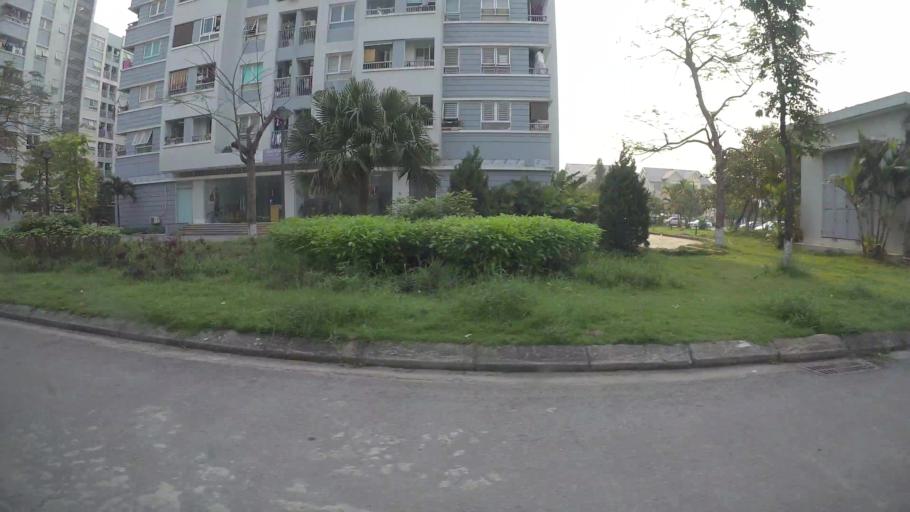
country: VN
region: Ha Noi
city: Ha Dong
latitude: 20.9971
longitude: 105.7478
